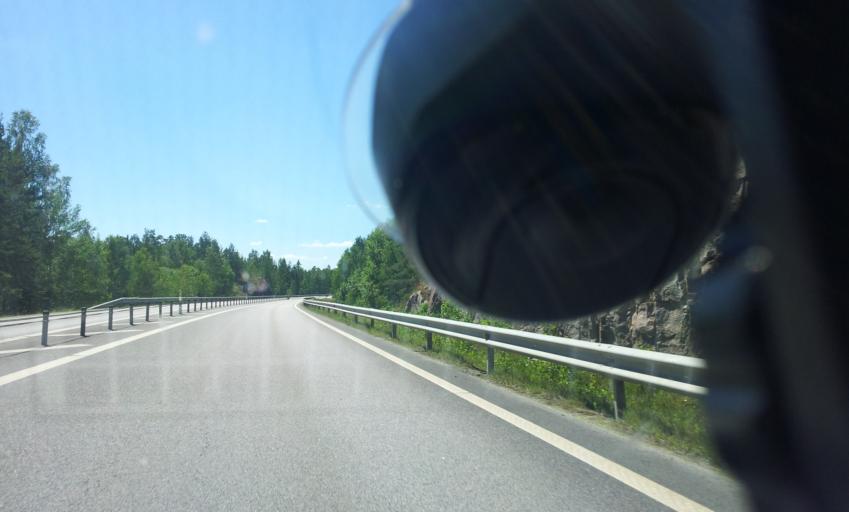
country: SE
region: OEstergoetland
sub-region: Valdemarsviks Kommun
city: Valdemarsvik
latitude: 58.1022
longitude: 16.5389
